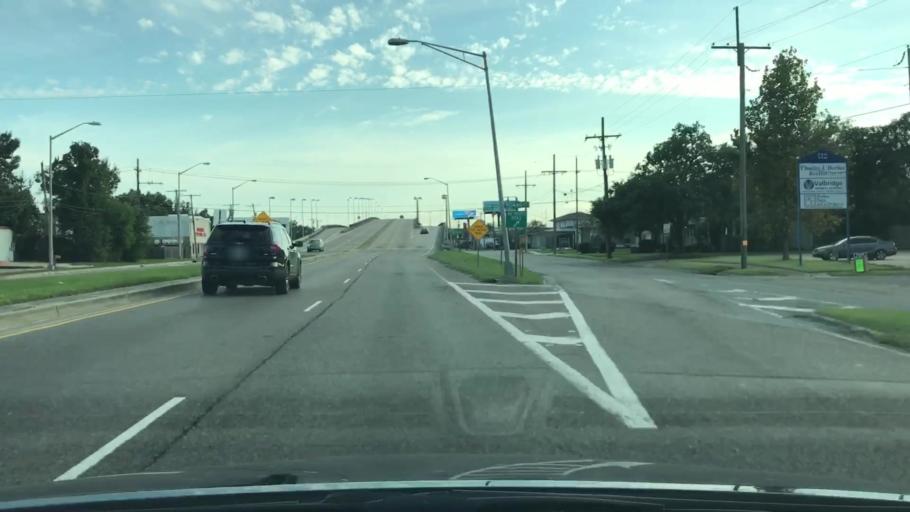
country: US
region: Louisiana
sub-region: Jefferson Parish
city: Metairie
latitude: 29.9791
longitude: -90.1563
